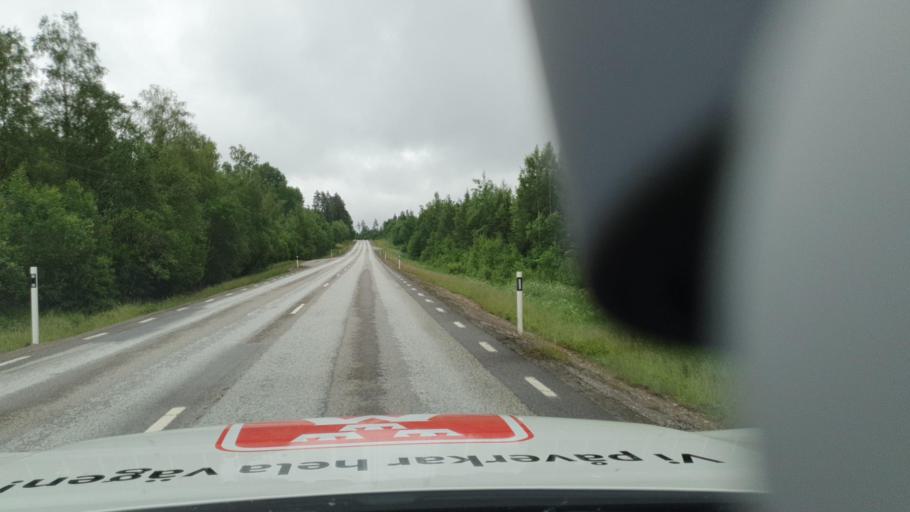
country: SE
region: Vaermland
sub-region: Kristinehamns Kommun
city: Bjorneborg
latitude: 59.2465
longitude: 14.2140
